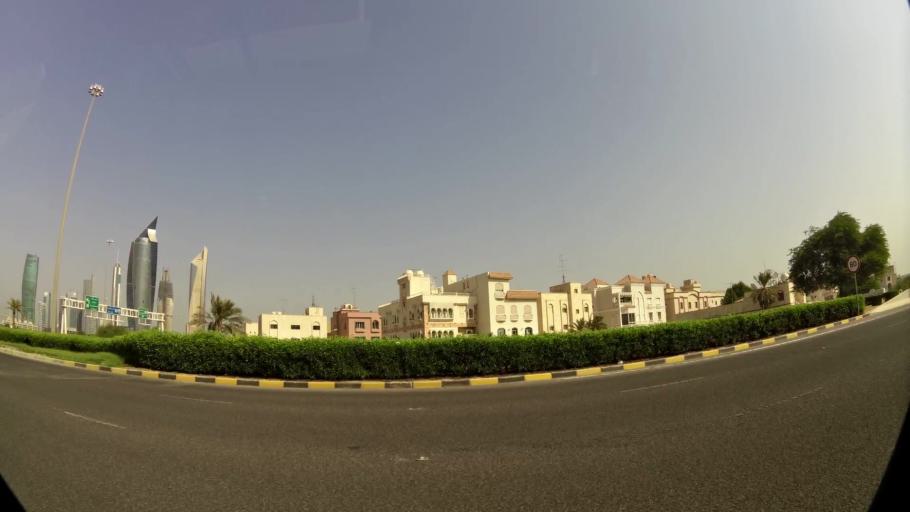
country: KW
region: Al Asimah
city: Ad Dasmah
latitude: 29.3636
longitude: 47.9936
